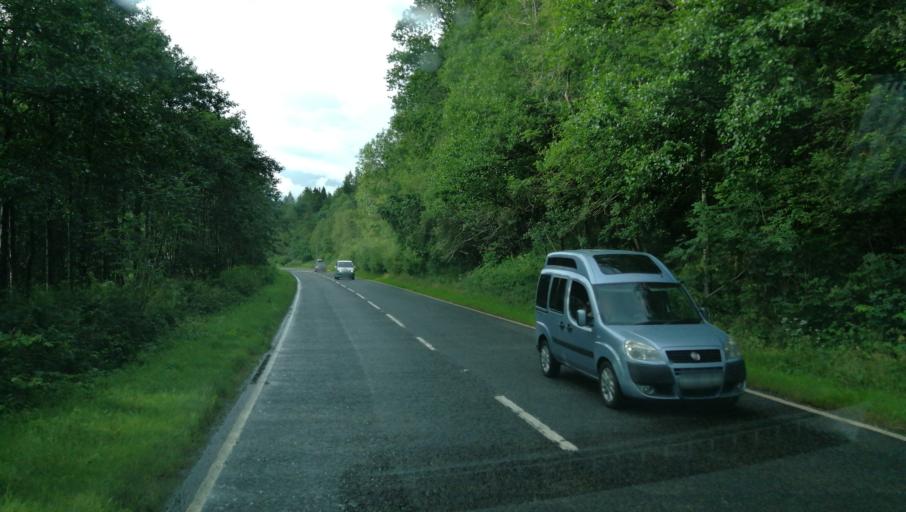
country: GB
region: Scotland
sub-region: Stirling
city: Callander
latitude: 56.3084
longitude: -4.3232
